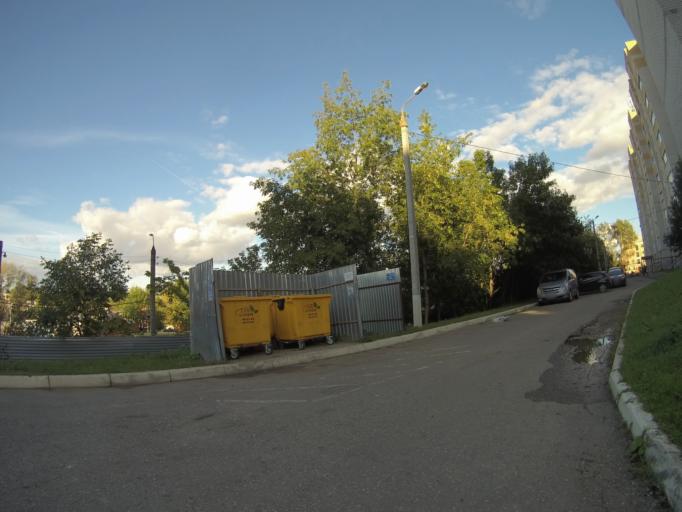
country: RU
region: Vladimir
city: Vladimir
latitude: 56.1530
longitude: 40.3766
